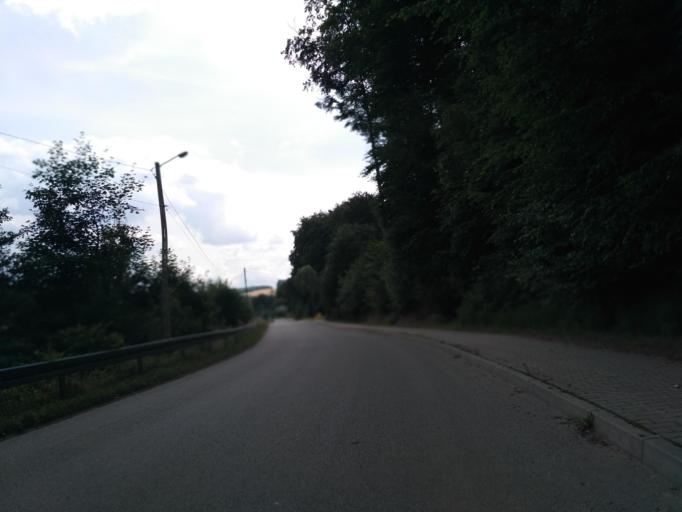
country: PL
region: Subcarpathian Voivodeship
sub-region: Powiat debicki
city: Brzeznica
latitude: 50.0460
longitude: 21.4869
